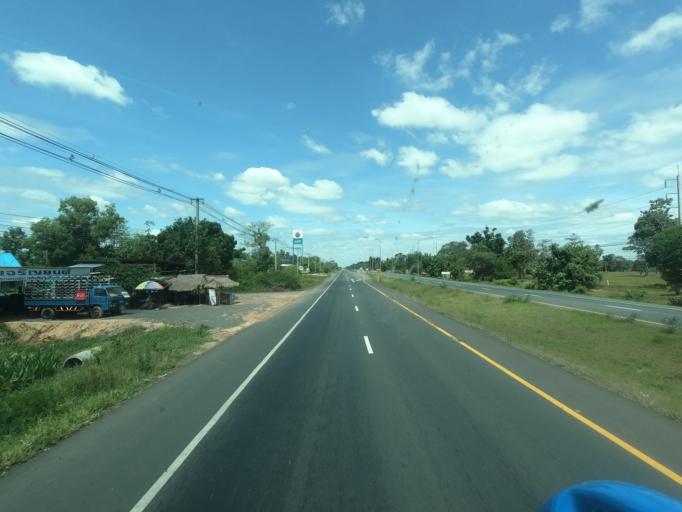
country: TH
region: Surin
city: Prasat
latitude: 14.6249
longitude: 103.3871
